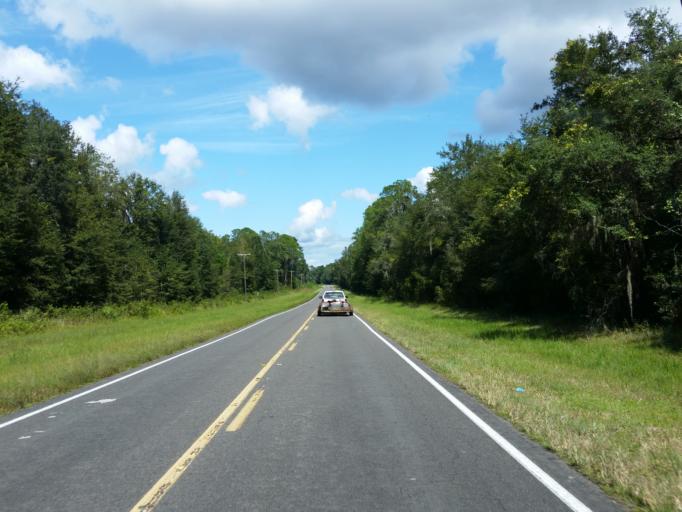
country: US
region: Florida
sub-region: Alachua County
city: Gainesville
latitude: 29.5324
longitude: -82.2710
